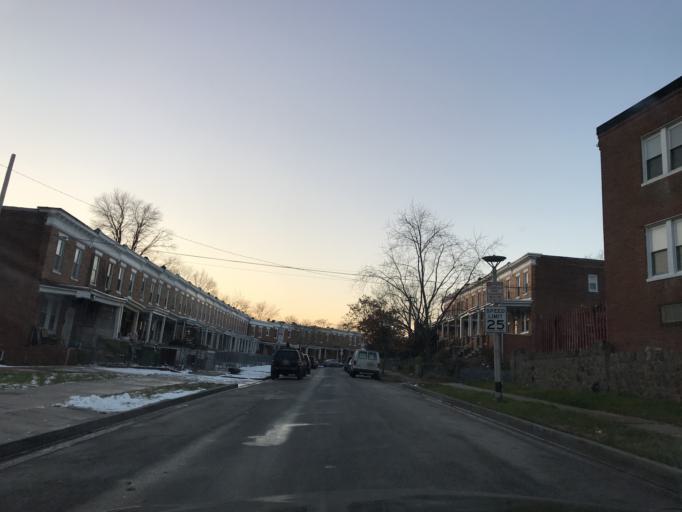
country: US
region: Maryland
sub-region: City of Baltimore
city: Baltimore
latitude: 39.3246
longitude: -76.5937
